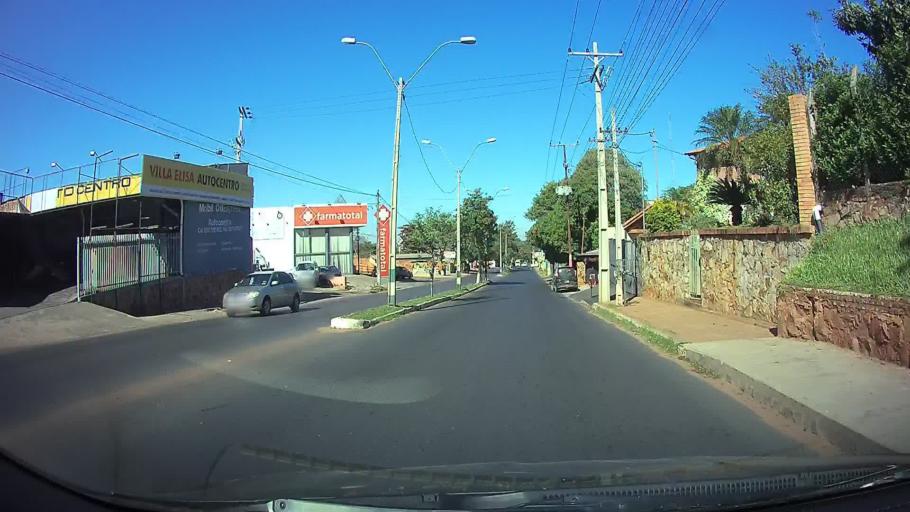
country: PY
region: Central
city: Villa Elisa
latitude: -25.3727
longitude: -57.5789
